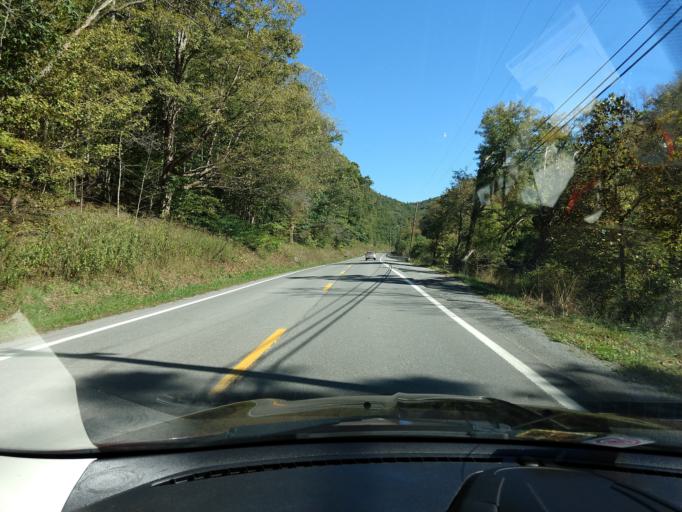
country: US
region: West Virginia
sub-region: Pocahontas County
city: Marlinton
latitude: 38.2132
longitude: -80.0623
